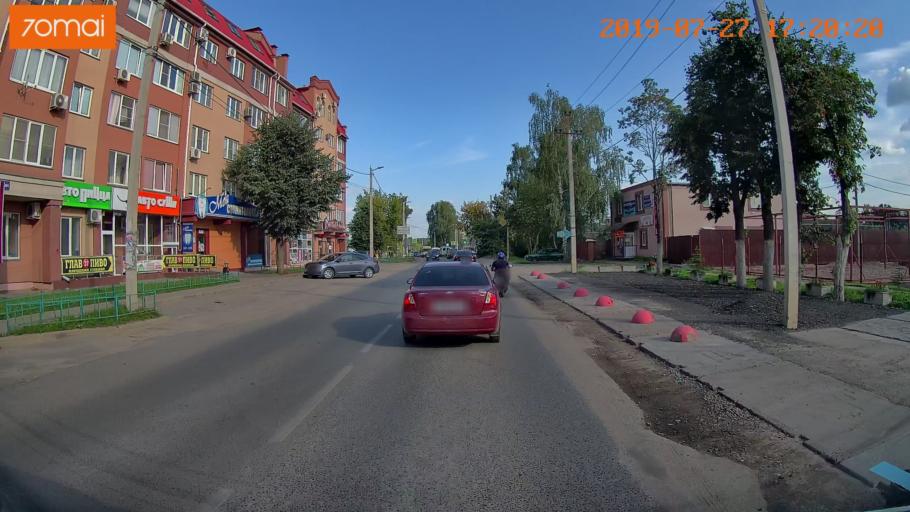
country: RU
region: Ivanovo
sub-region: Gorod Ivanovo
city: Ivanovo
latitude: 57.0310
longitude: 40.9219
